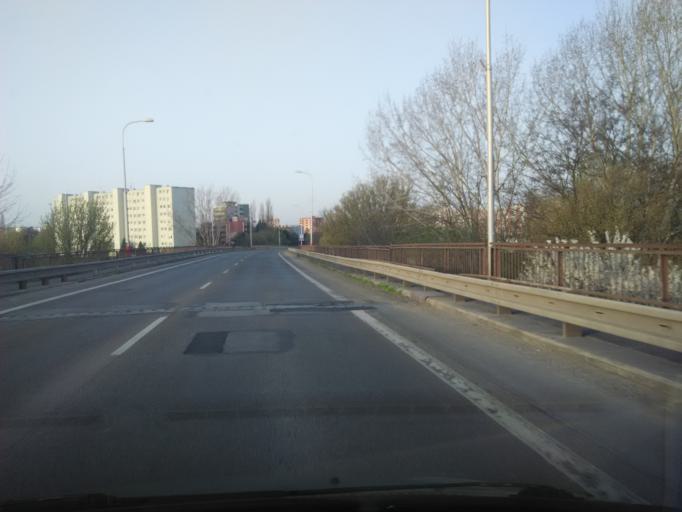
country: SK
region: Nitriansky
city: Sellye
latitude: 48.1595
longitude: 17.8792
